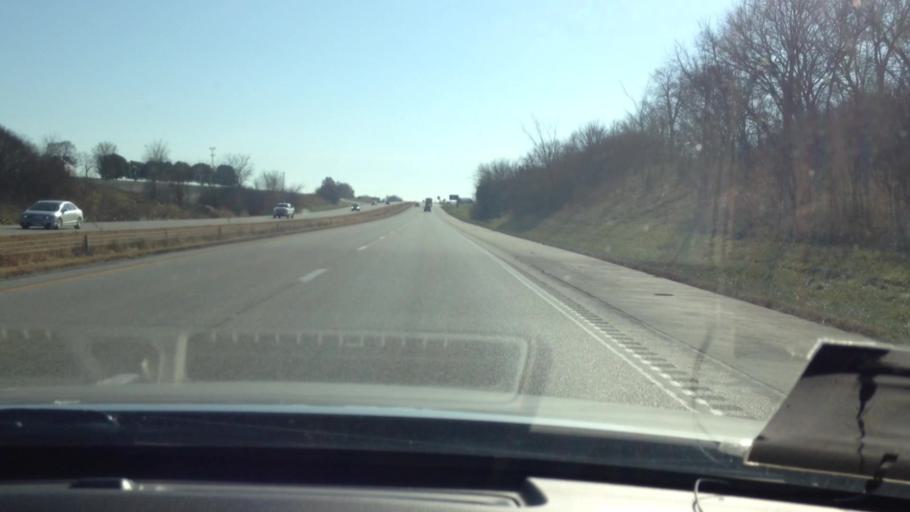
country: US
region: Missouri
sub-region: Platte County
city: Platte City
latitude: 39.4841
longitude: -94.7869
